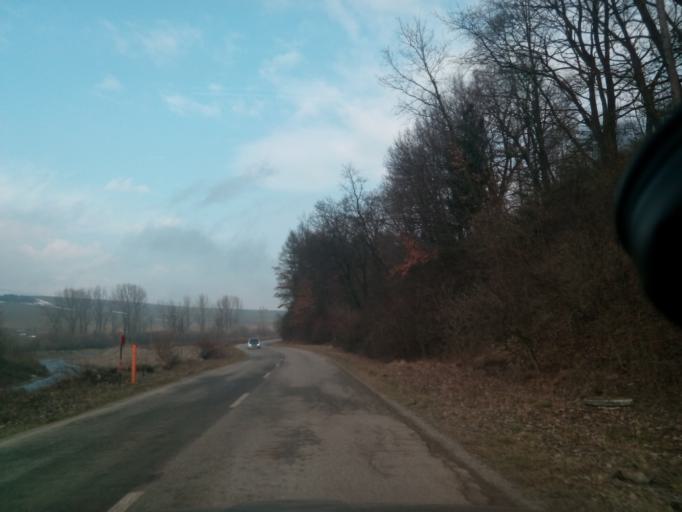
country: SK
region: Presovsky
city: Lipany
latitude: 49.1620
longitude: 20.8755
